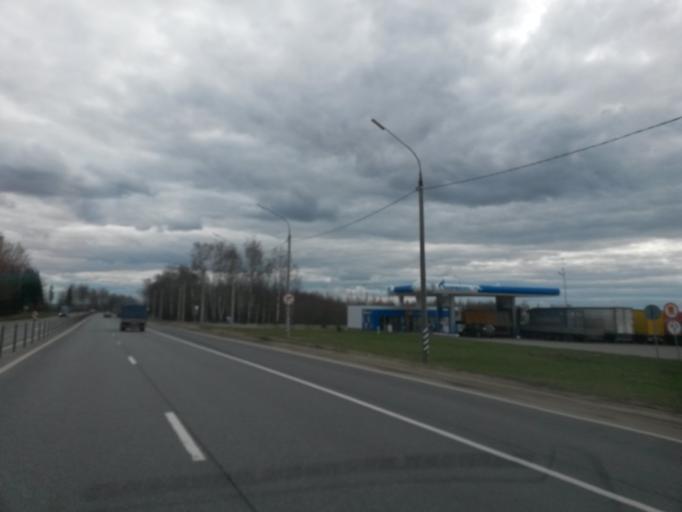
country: RU
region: Jaroslavl
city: Semibratovo
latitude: 57.3418
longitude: 39.5814
